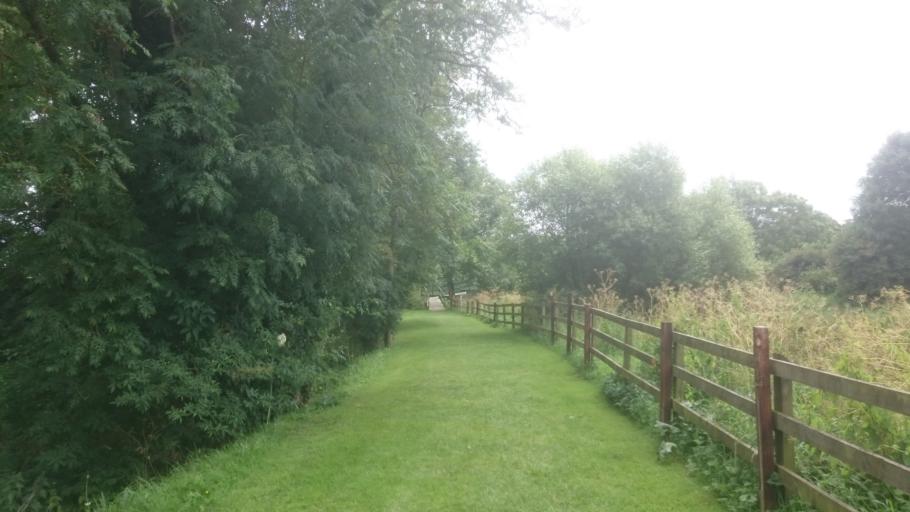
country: IE
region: Leinster
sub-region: Kilkenny
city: Kilkenny
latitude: 52.5399
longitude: -7.2673
